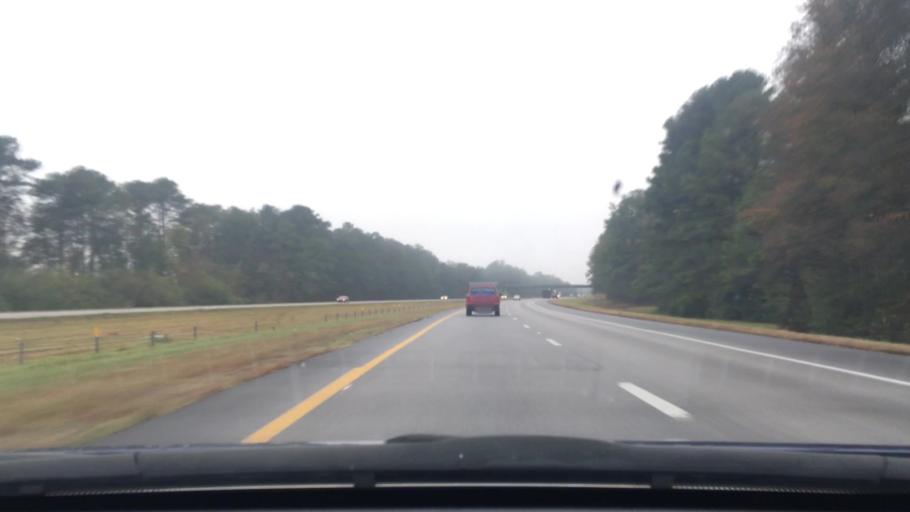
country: US
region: South Carolina
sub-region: Lee County
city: Bishopville
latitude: 34.1960
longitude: -80.3337
